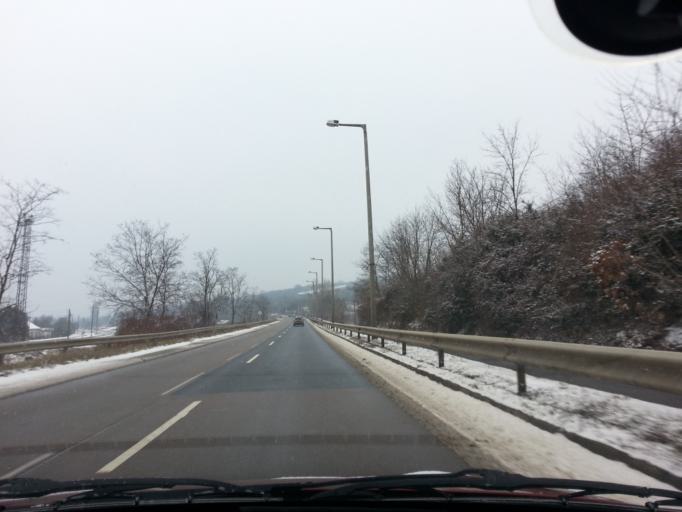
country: HU
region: Nograd
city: Salgotarjan
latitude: 48.0876
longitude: 19.7885
